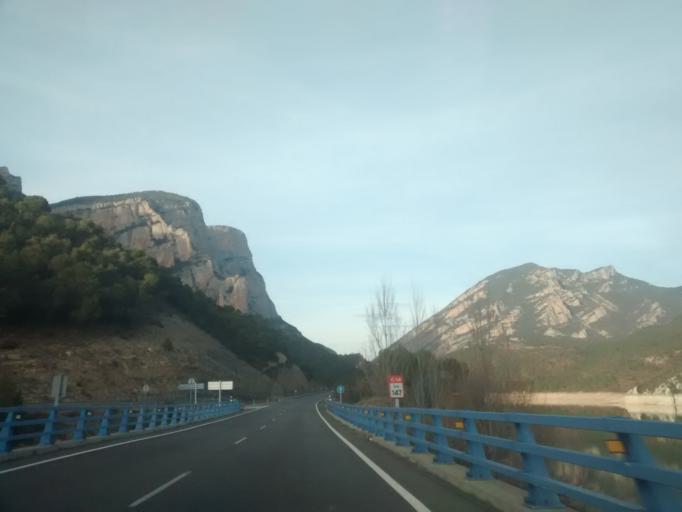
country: ES
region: Catalonia
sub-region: Provincia de Lleida
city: Oliana
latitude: 42.1073
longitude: 1.2995
